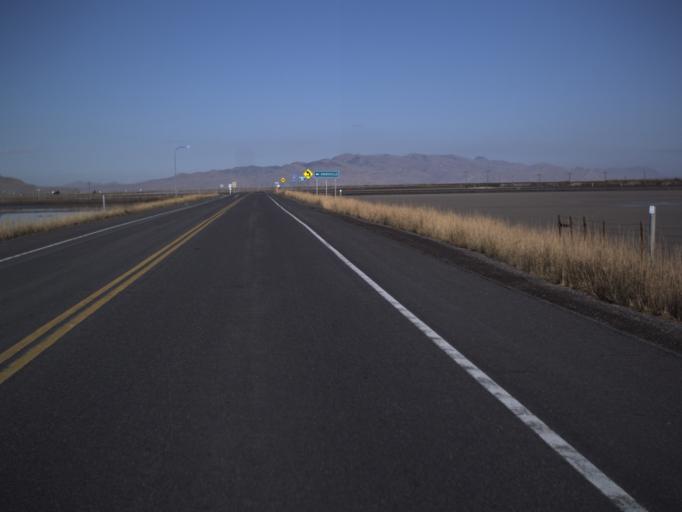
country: US
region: Utah
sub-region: Tooele County
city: Grantsville
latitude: 40.7097
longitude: -112.5236
